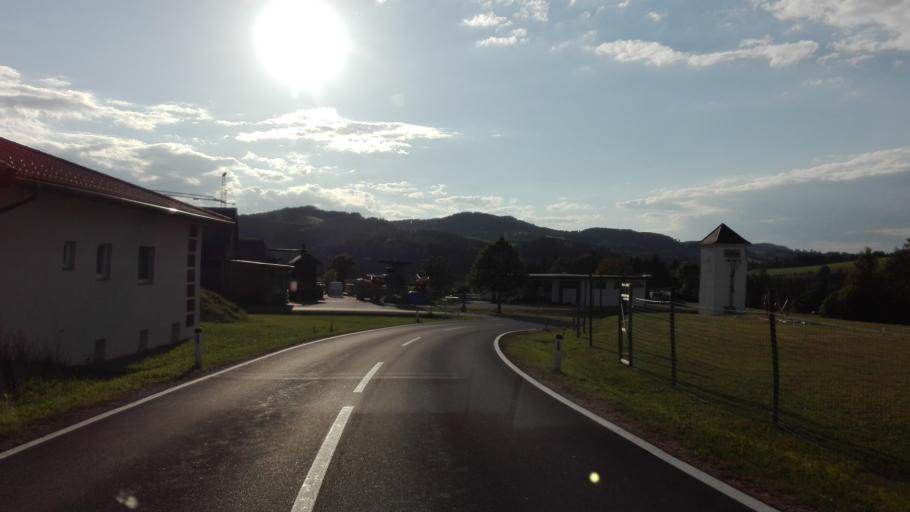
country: AT
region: Upper Austria
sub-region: Politischer Bezirk Urfahr-Umgebung
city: Engerwitzdorf
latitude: 48.3939
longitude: 14.5570
